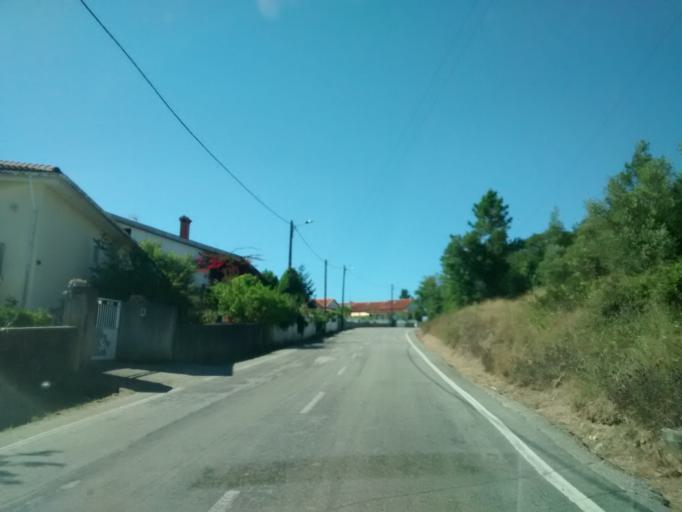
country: PT
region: Aveiro
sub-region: Anadia
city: Sangalhos
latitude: 40.4403
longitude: -8.5004
